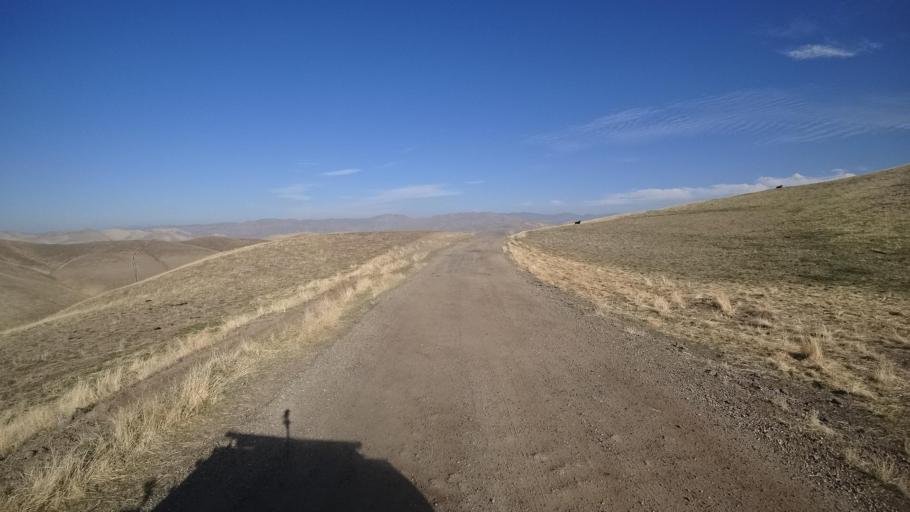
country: US
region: California
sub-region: Kern County
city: Oildale
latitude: 35.4910
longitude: -118.8800
